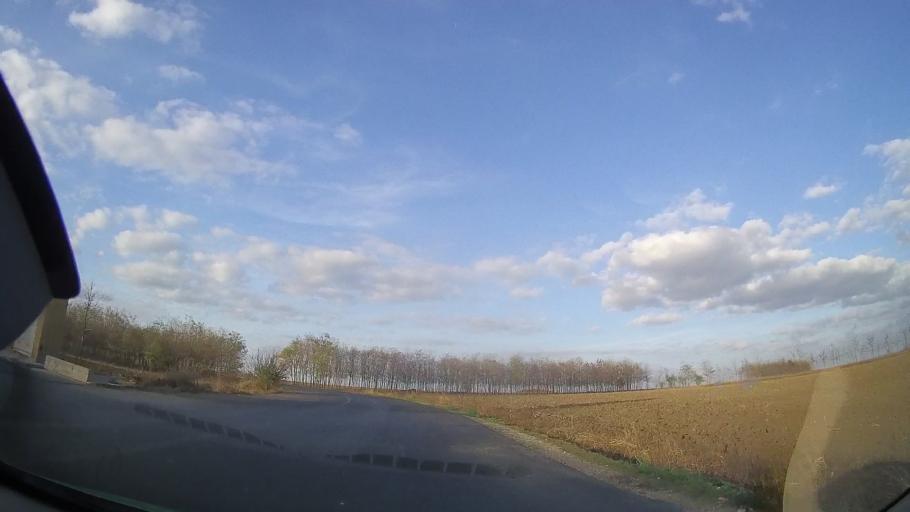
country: RO
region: Constanta
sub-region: Comuna Dumbraveni
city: Dumbraveni
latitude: 43.9276
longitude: 28.0298
